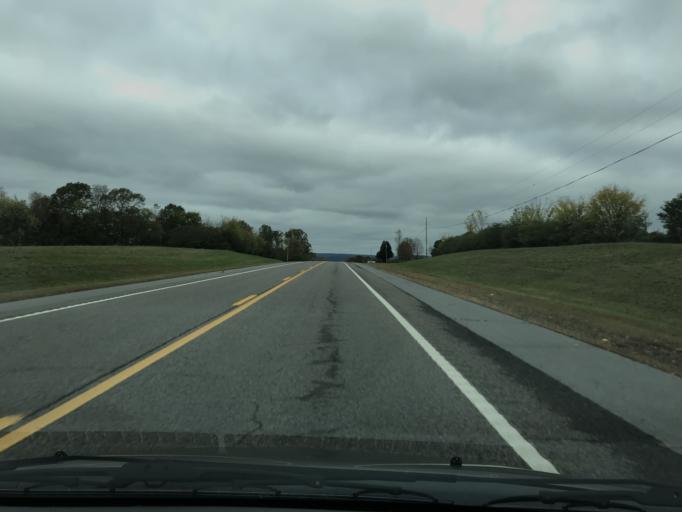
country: US
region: Tennessee
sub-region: Rhea County
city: Graysville
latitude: 35.3866
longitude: -85.0043
